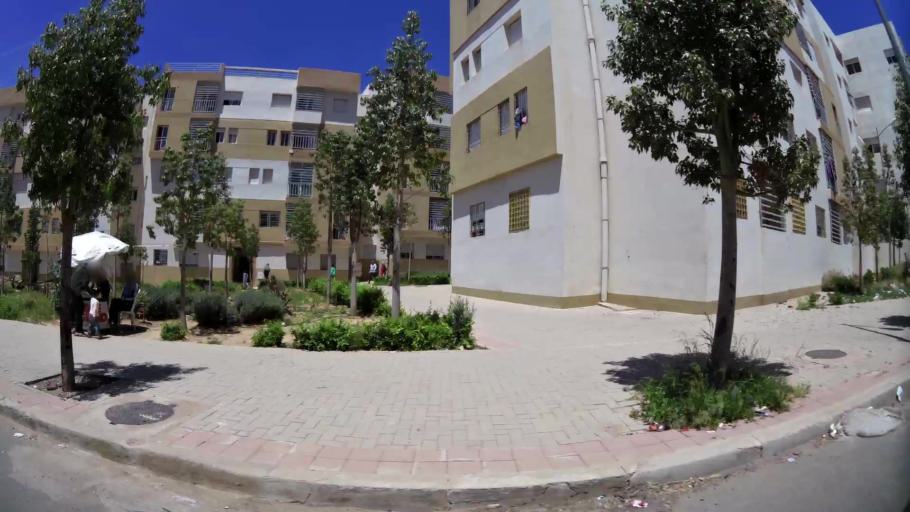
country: MA
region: Oriental
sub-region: Oujda-Angad
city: Oujda
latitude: 34.6644
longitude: -1.9226
